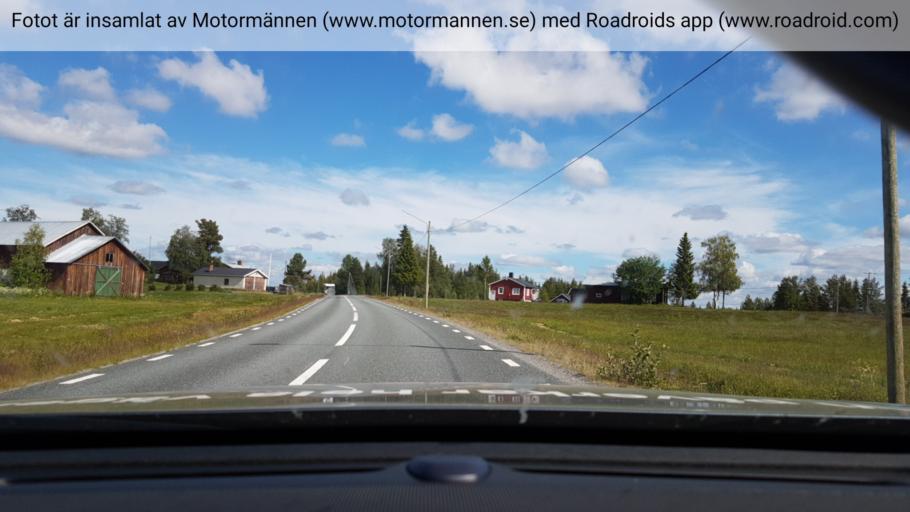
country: SE
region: Vaesterbotten
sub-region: Sorsele Kommun
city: Sorsele
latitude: 65.5562
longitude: 17.8482
